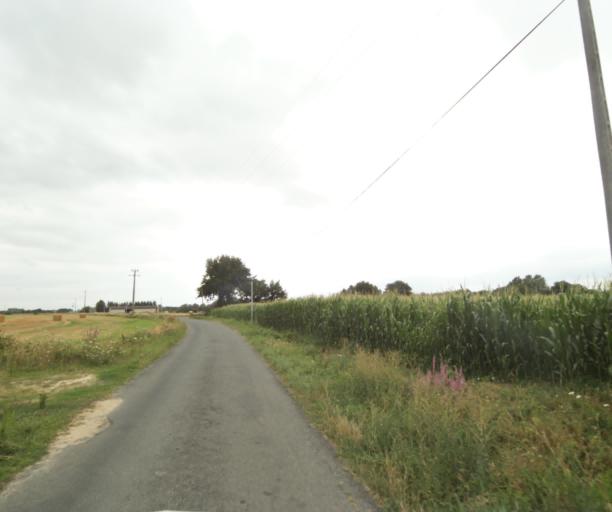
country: FR
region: Pays de la Loire
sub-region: Departement de la Sarthe
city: Sable-sur-Sarthe
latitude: 47.8107
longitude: -0.3796
